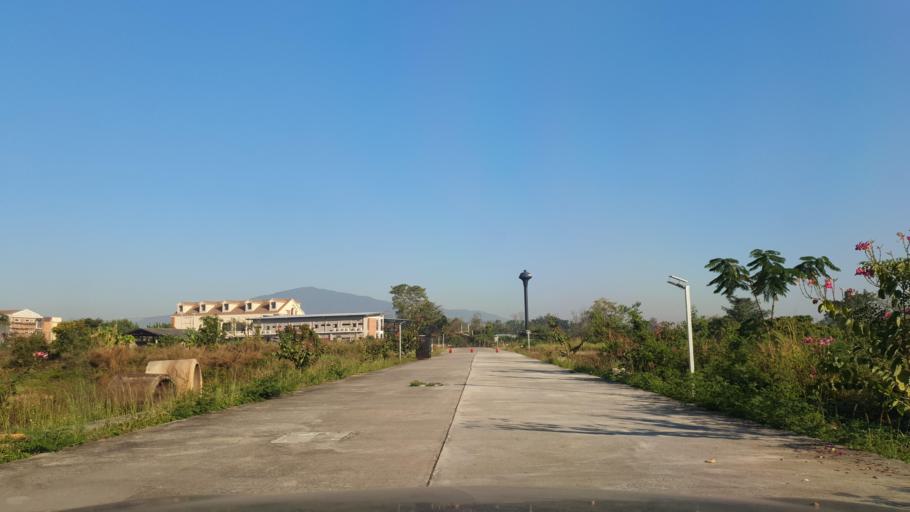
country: TH
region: Chiang Mai
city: Hang Dong
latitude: 18.6946
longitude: 98.9680
